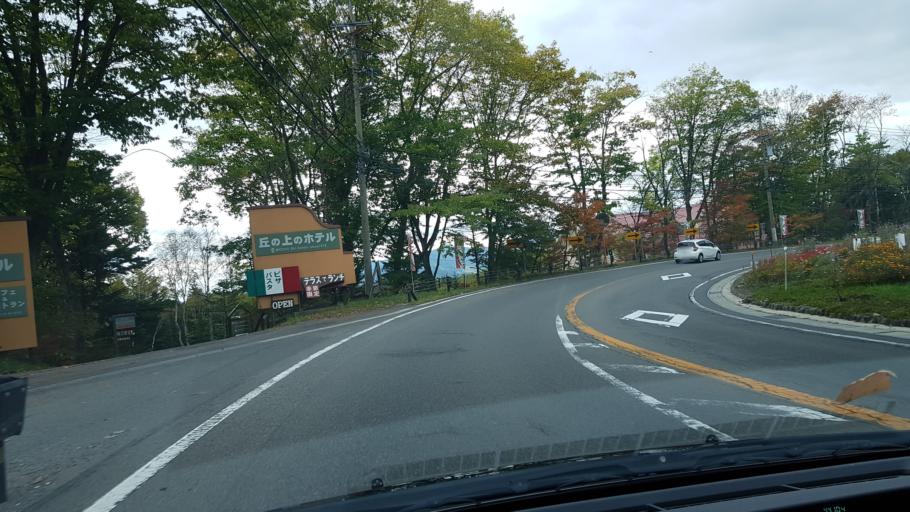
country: JP
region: Gunma
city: Nakanojomachi
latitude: 36.6083
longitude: 138.5843
